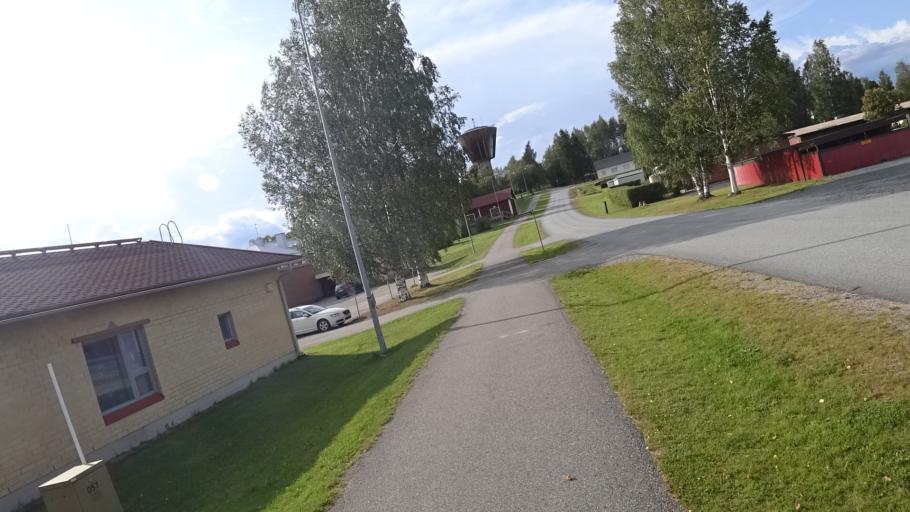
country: FI
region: North Karelia
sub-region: Joensuu
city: Ilomantsi
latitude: 62.6697
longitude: 30.9228
